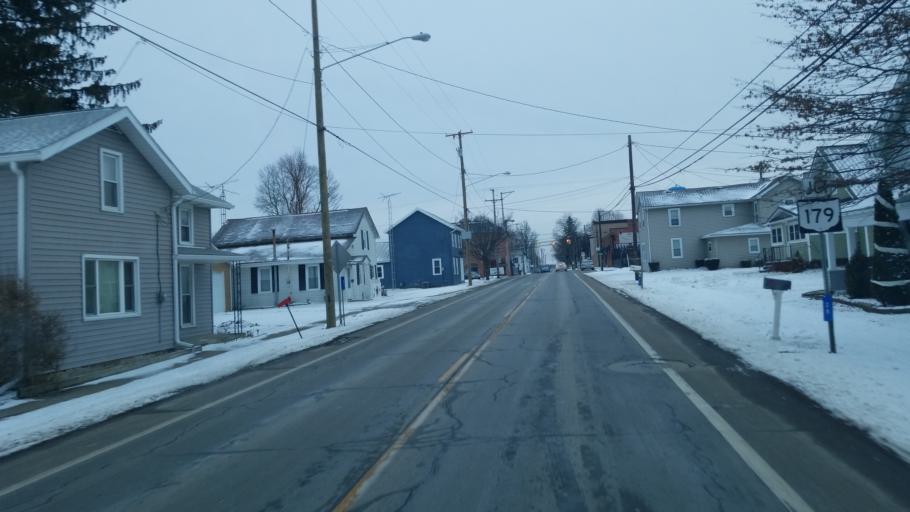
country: US
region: Ohio
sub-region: Ashland County
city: Ashland
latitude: 40.7744
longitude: -82.2622
